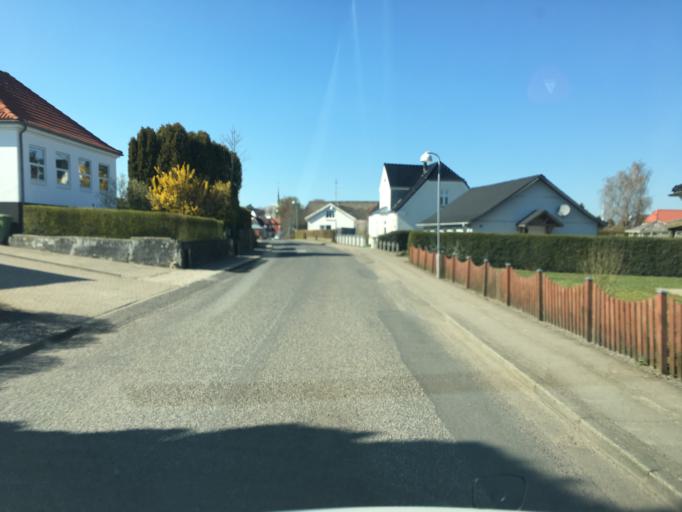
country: DK
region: South Denmark
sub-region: Aabenraa Kommune
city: Krusa
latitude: 54.9365
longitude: 9.4046
